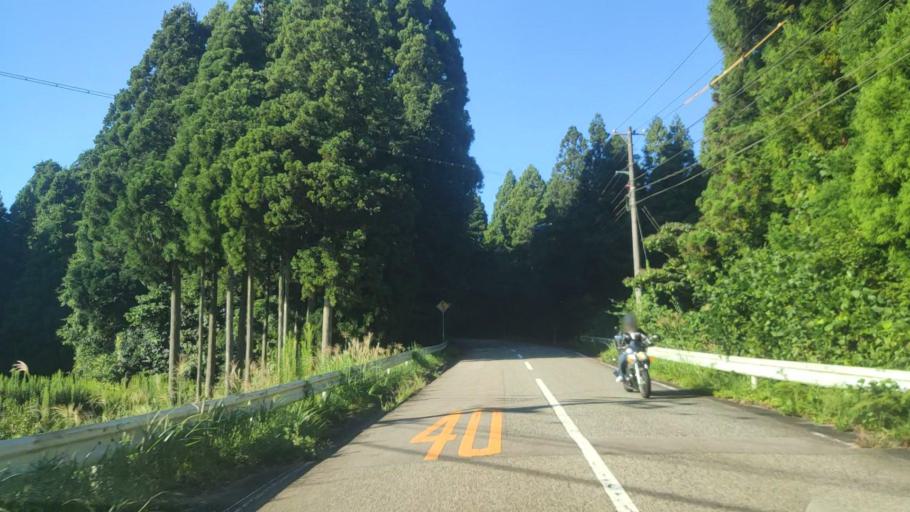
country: JP
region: Ishikawa
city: Nanao
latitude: 37.1095
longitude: 136.9618
